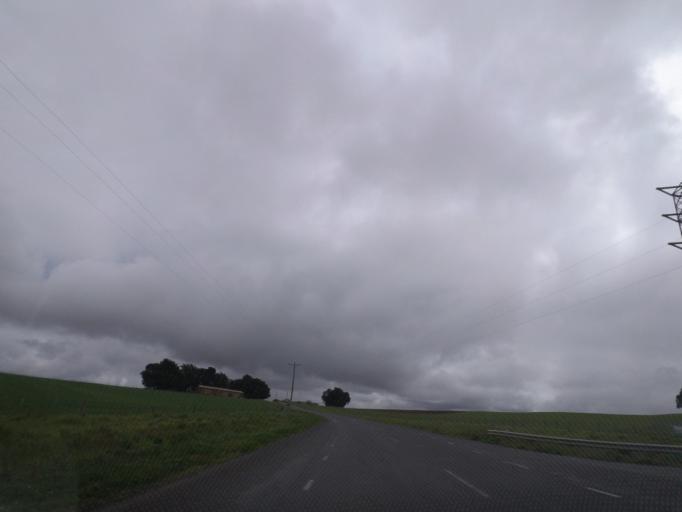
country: AU
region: Victoria
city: Brown Hill
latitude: -37.5775
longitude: 143.9510
